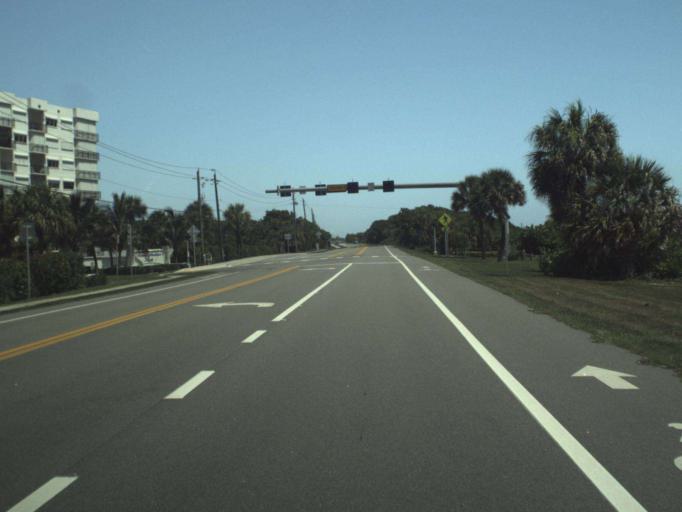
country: US
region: Florida
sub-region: Indian River County
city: South Beach
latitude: 27.5330
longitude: -80.3148
